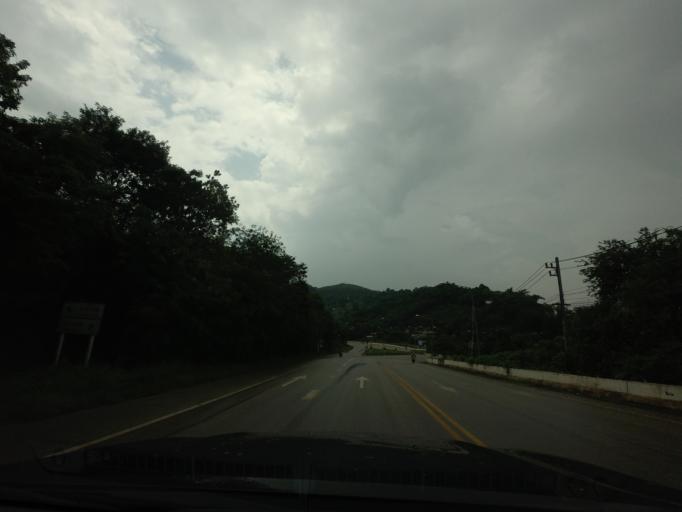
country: TH
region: Loei
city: Pak Chom
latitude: 18.1207
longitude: 101.9979
